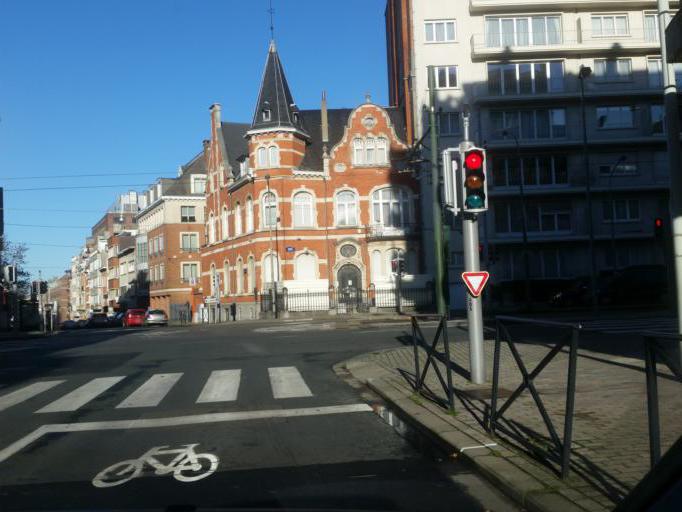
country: BE
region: Brussels Capital
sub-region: Bruxelles-Capitale
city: Brussels
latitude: 50.8112
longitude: 4.3576
